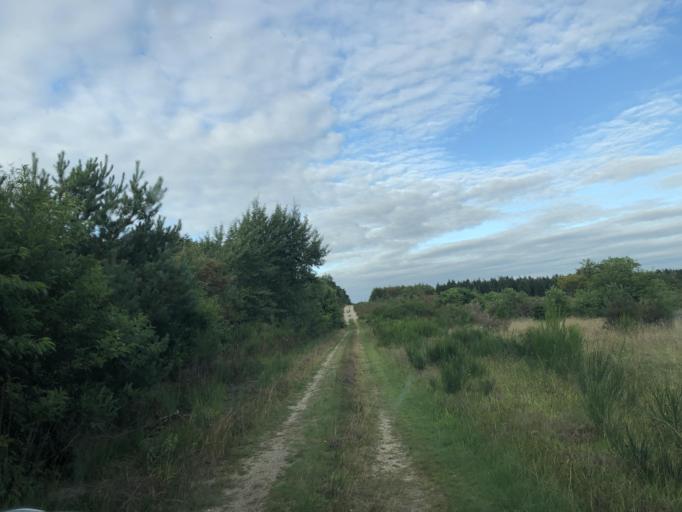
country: DK
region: Central Jutland
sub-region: Holstebro Kommune
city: Ulfborg
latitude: 56.2881
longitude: 8.4176
